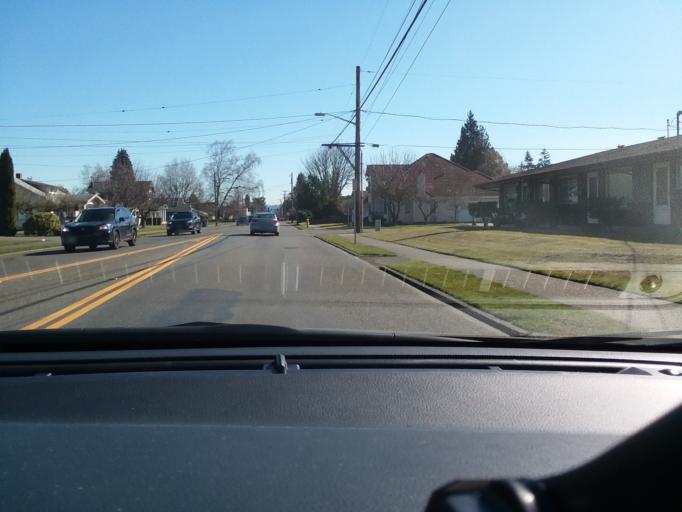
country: US
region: Washington
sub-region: Pierce County
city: Puyallup
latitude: 47.1903
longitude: -122.3139
